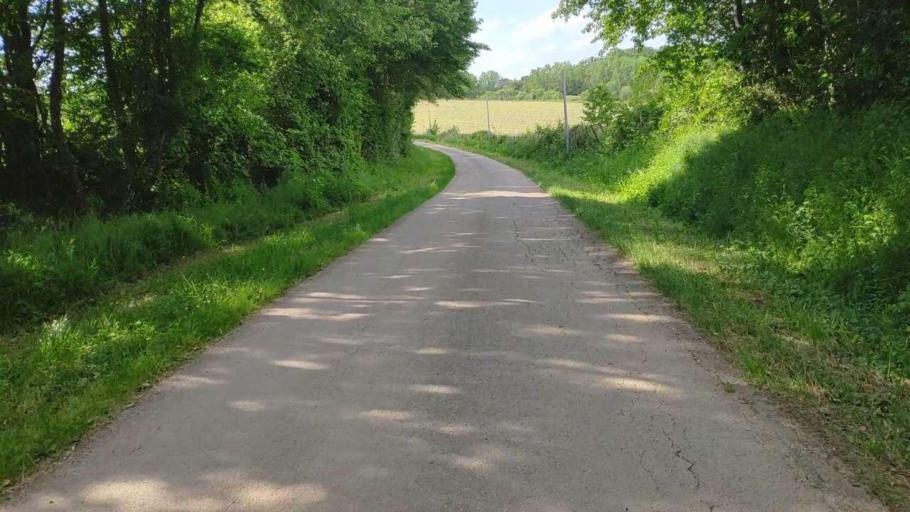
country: FR
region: Franche-Comte
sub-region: Departement du Jura
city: Bletterans
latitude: 46.8213
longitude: 5.3654
